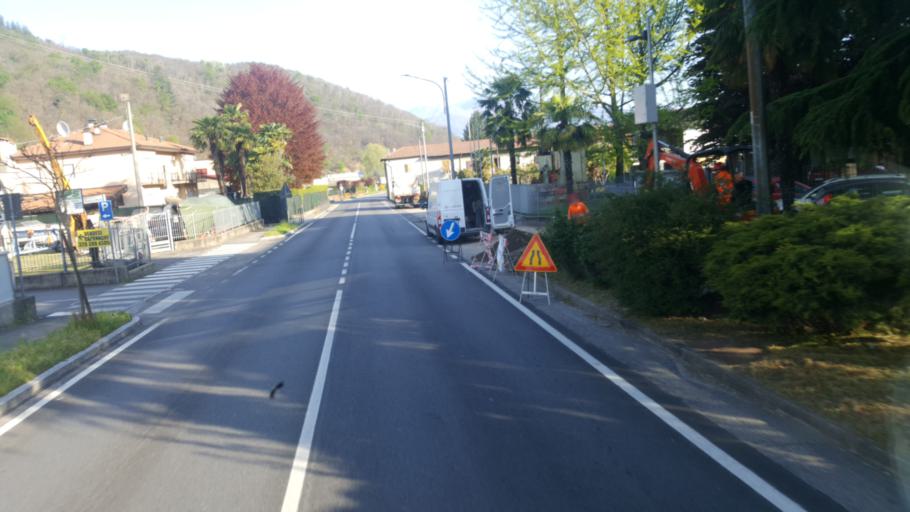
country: IT
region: Lombardy
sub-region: Provincia di Varese
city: Montegrino Valtravaglia
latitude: 45.9653
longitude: 8.7526
